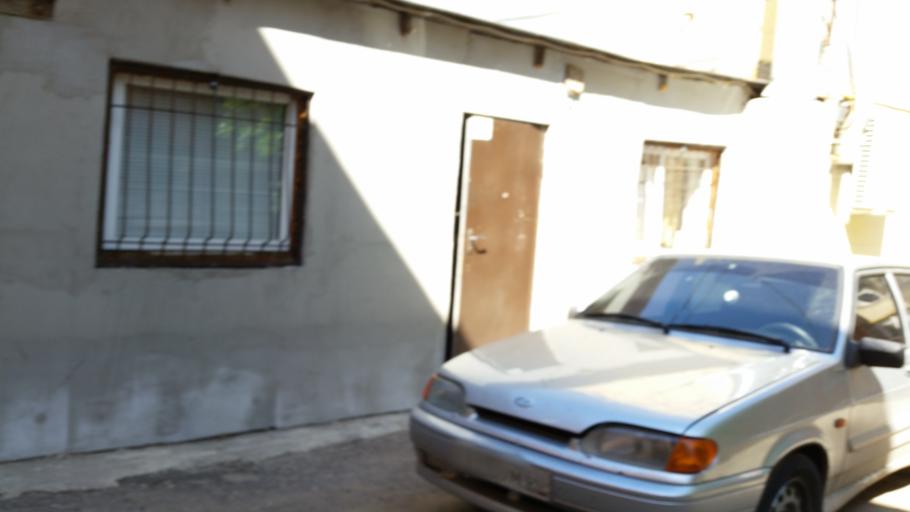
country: RU
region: Saratov
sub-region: Saratovskiy Rayon
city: Saratov
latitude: 51.5290
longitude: 46.0394
